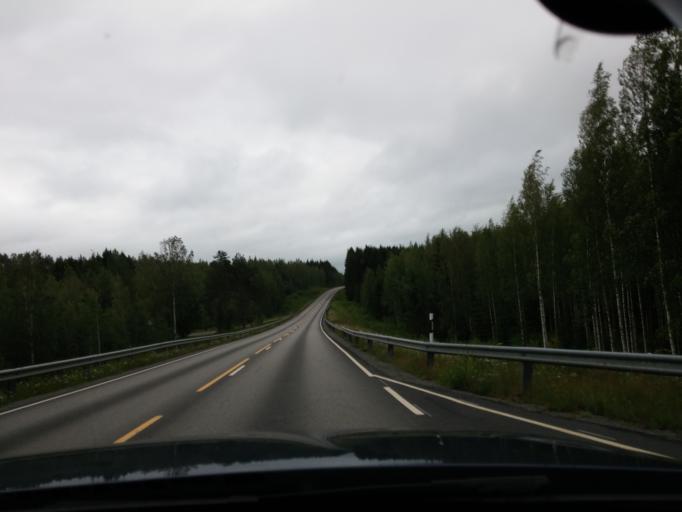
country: FI
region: Central Finland
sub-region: Saarijaervi-Viitasaari
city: Saarijaervi
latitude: 62.6834
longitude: 25.2425
